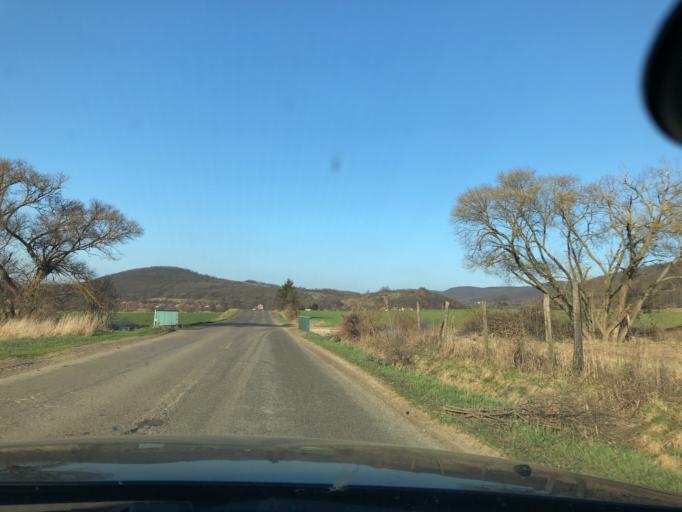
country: HU
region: Nograd
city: Bujak
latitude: 47.9611
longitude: 19.6013
